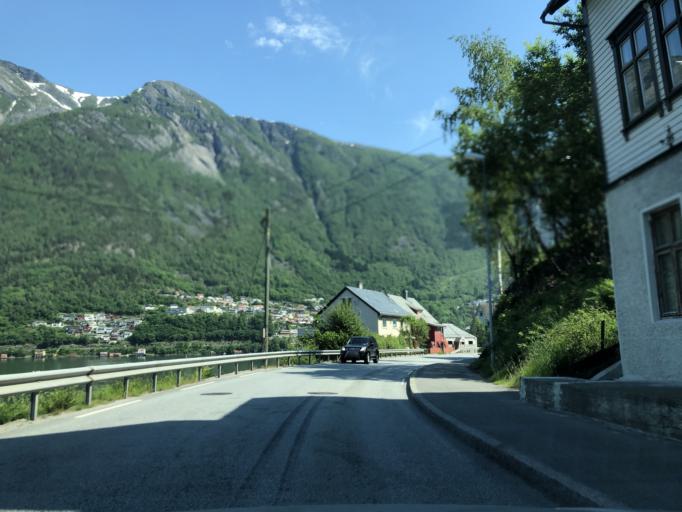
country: NO
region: Hordaland
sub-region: Odda
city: Odda
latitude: 60.0753
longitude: 6.5359
